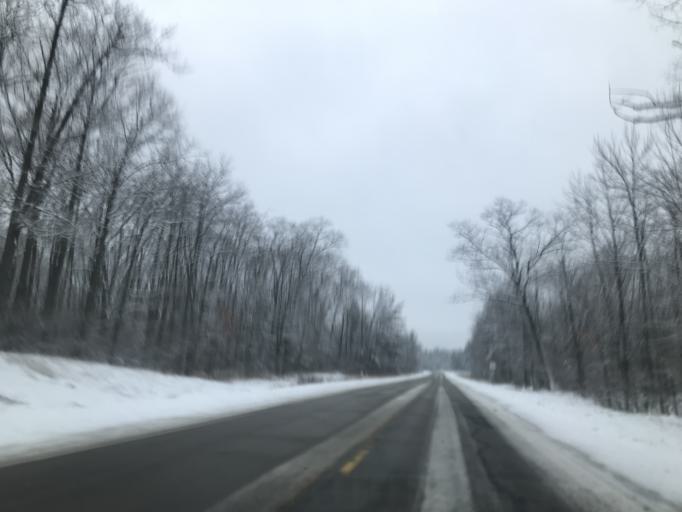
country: US
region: Wisconsin
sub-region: Oconto County
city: Oconto Falls
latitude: 44.8628
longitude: -88.1174
